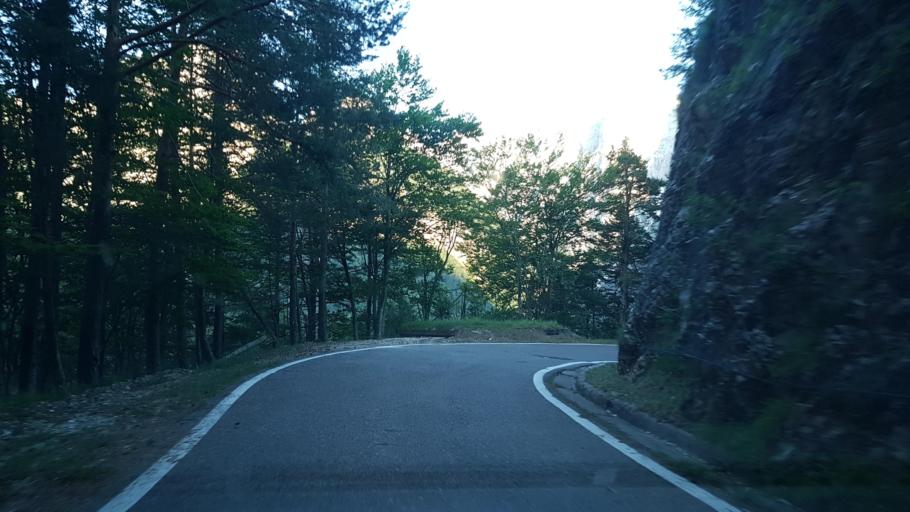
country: IT
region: Friuli Venezia Giulia
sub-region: Provincia di Udine
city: Dogna
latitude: 46.4557
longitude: 13.3769
